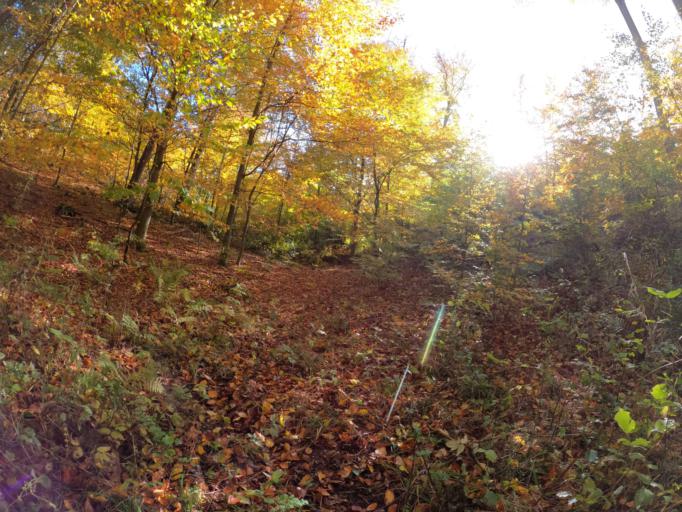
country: PL
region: West Pomeranian Voivodeship
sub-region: Powiat mysliborski
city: Barlinek
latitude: 52.9729
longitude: 15.2241
